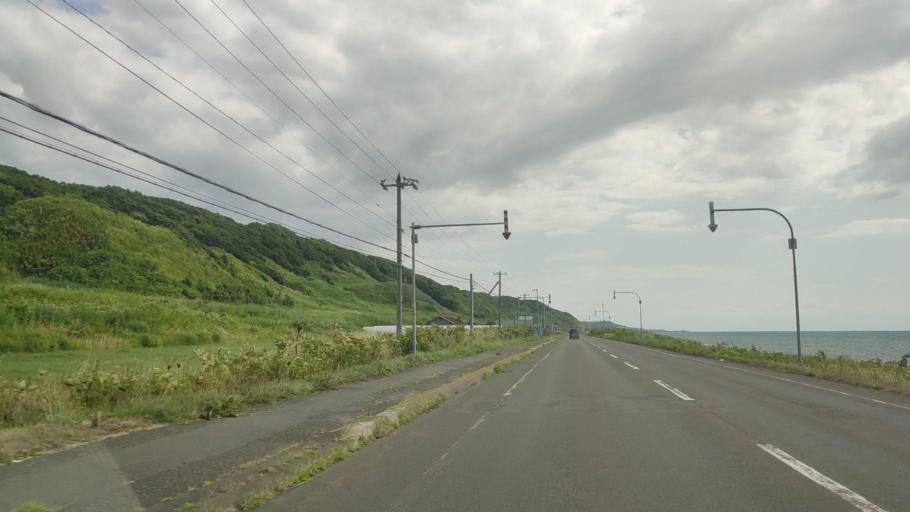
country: JP
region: Hokkaido
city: Rumoi
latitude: 44.1877
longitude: 141.6586
